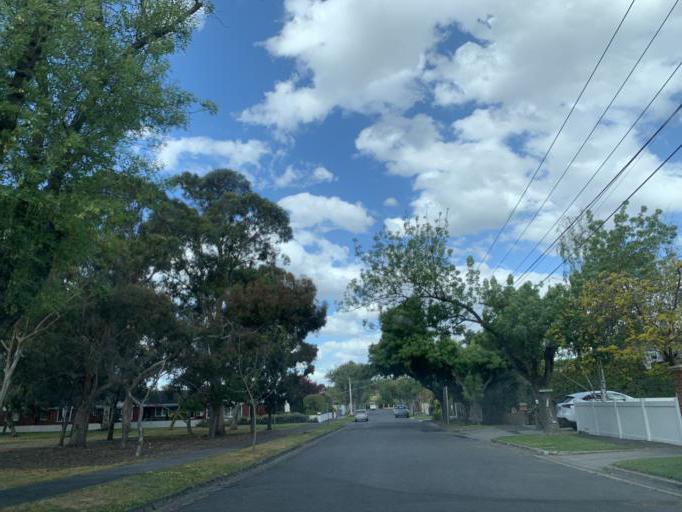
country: AU
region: Victoria
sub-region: Bayside
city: Hampton
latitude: -37.9237
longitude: 145.0085
